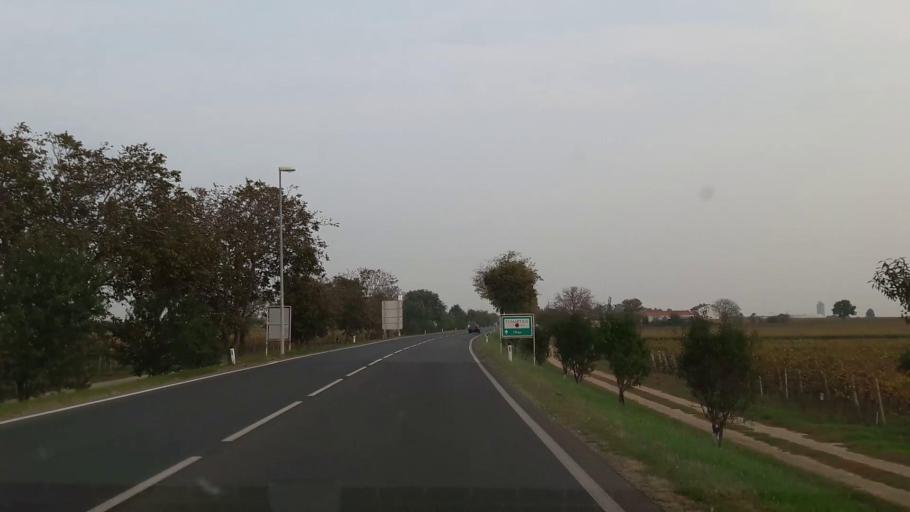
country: AT
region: Burgenland
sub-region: Politischer Bezirk Neusiedl am See
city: Weiden am See
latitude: 47.9115
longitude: 16.8894
